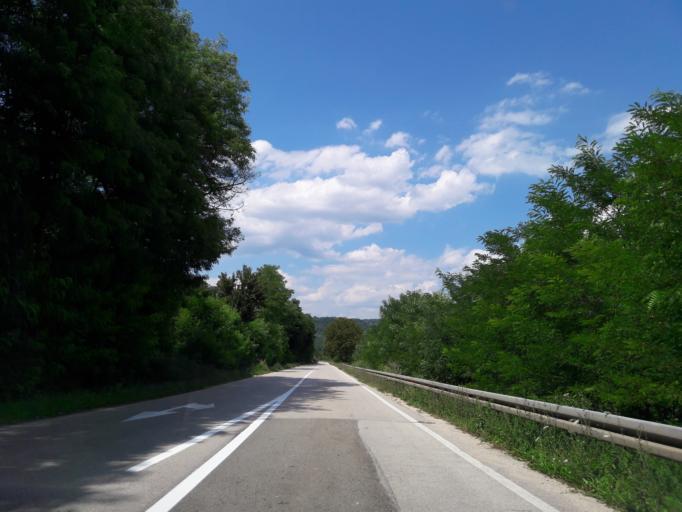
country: BA
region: Republika Srpska
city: Mrkonjic Grad
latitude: 44.5286
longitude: 17.1507
